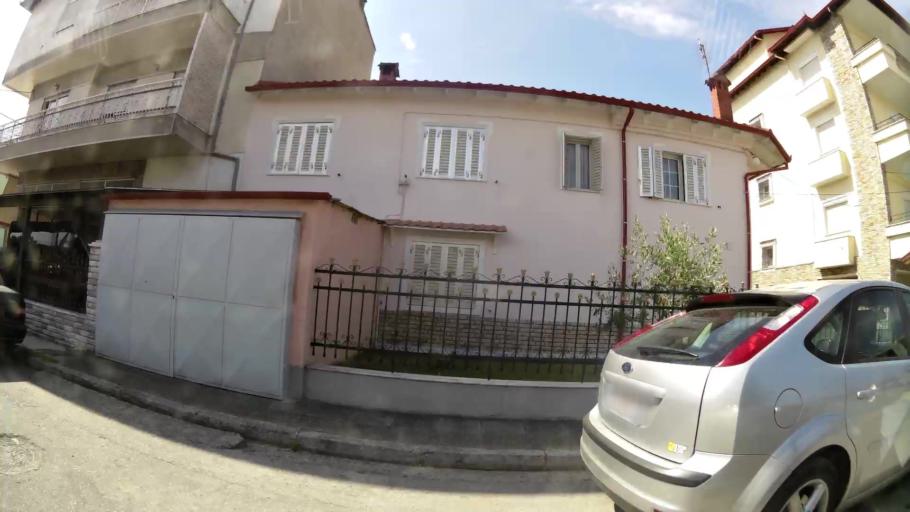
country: GR
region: Central Macedonia
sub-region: Nomos Pierias
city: Katerini
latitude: 40.2710
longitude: 22.4912
